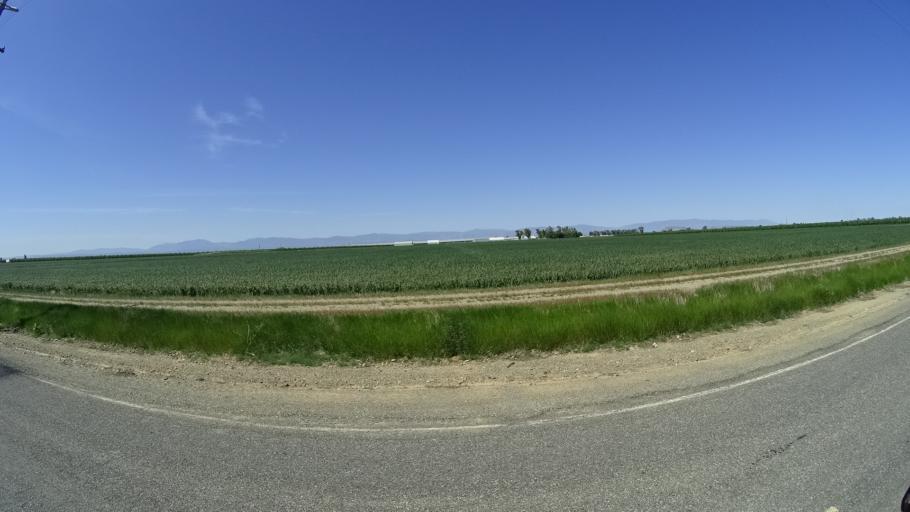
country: US
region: California
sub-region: Glenn County
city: Orland
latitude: 39.6792
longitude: -122.1781
